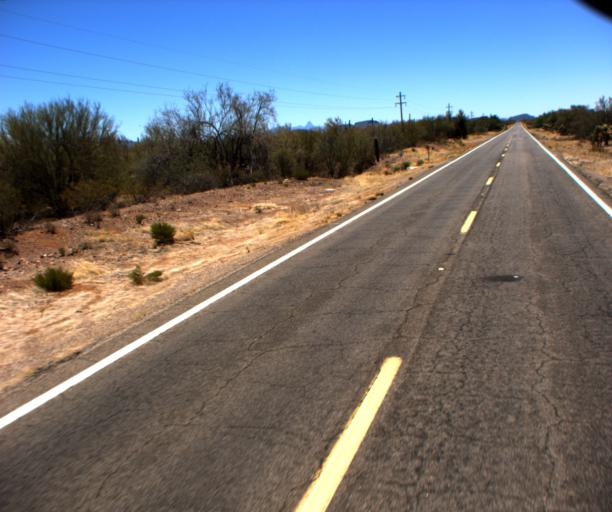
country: US
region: Arizona
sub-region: Pima County
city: Sells
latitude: 32.0445
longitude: -112.0209
